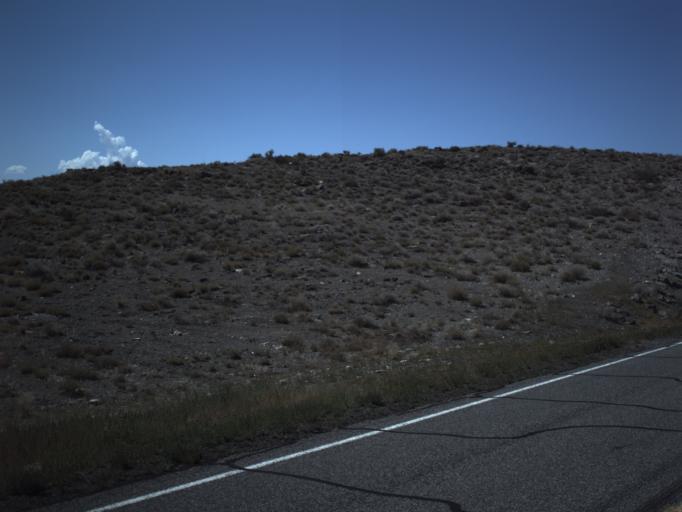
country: US
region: Utah
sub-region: Beaver County
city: Milford
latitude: 39.0345
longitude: -113.3404
